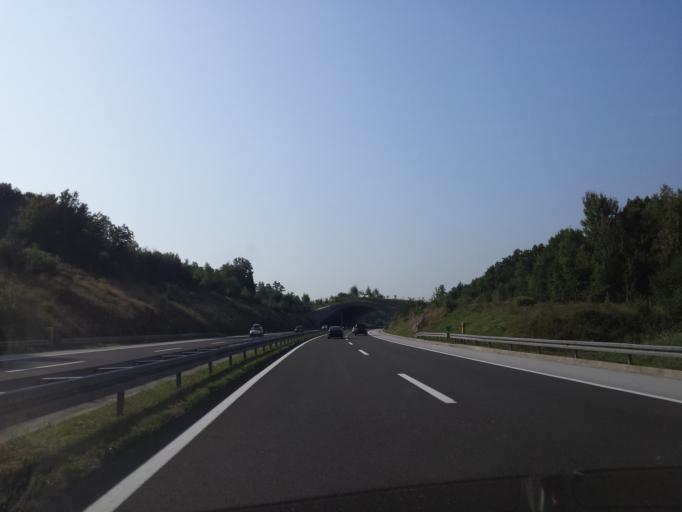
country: HR
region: Karlovacka
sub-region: Grad Ogulin
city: Ogulin
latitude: 45.3764
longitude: 15.2685
